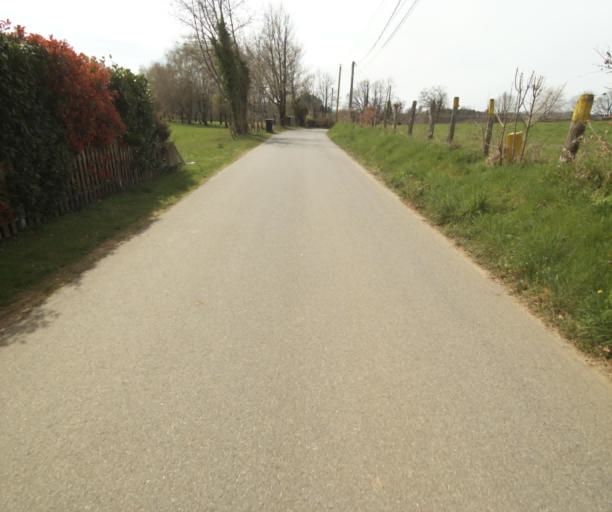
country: FR
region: Limousin
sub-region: Departement de la Correze
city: Naves
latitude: 45.3054
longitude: 1.7665
